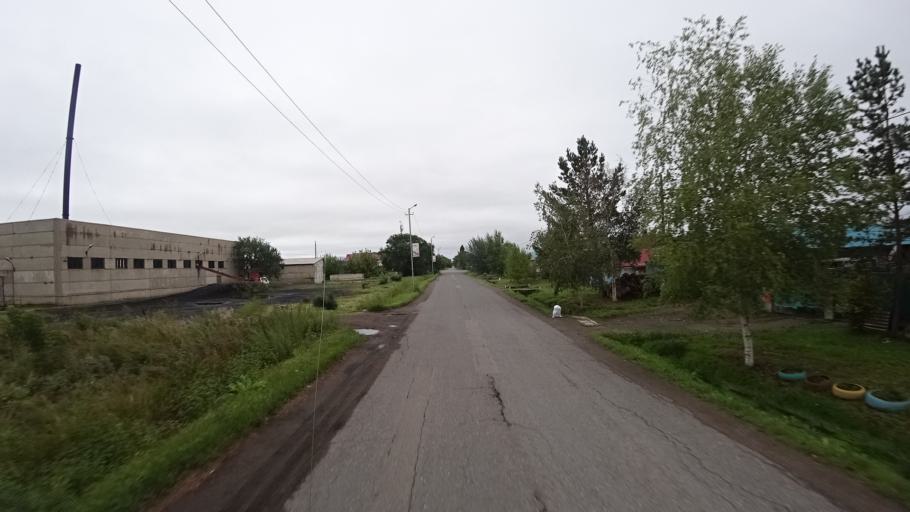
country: RU
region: Primorskiy
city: Chernigovka
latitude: 44.3367
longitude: 132.5814
